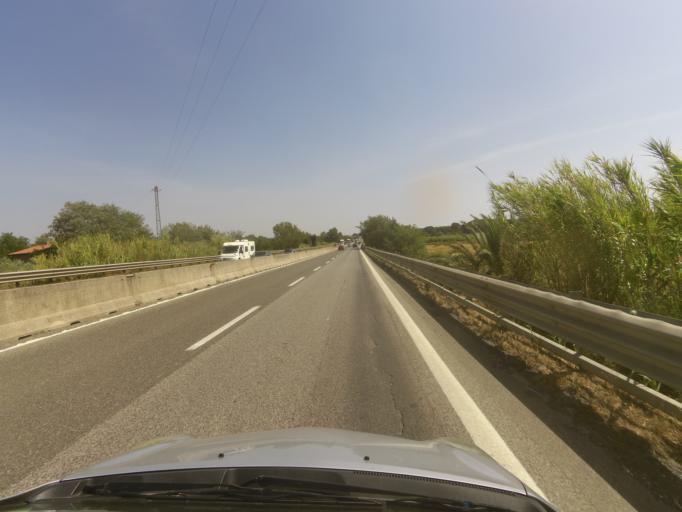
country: IT
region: Tuscany
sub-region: Provincia di Livorno
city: S.P. in Palazzi
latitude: 43.3265
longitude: 10.5289
